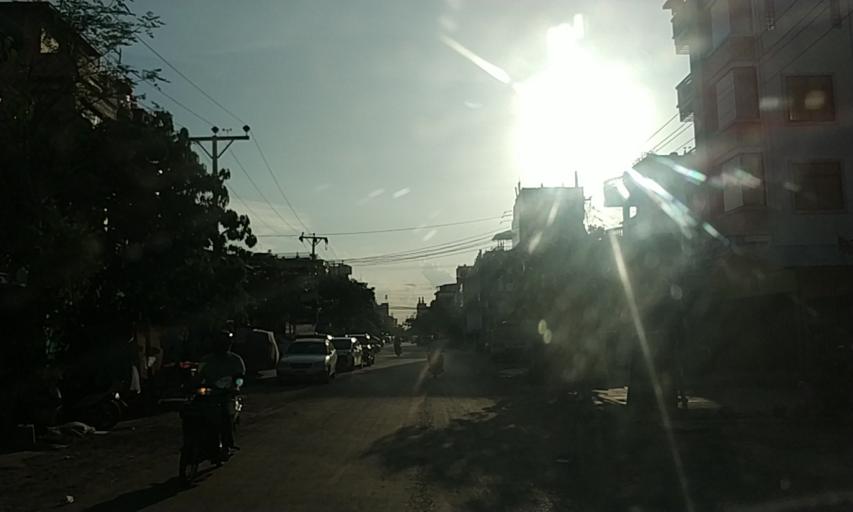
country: MM
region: Mandalay
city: Mandalay
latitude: 21.9702
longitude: 96.0961
